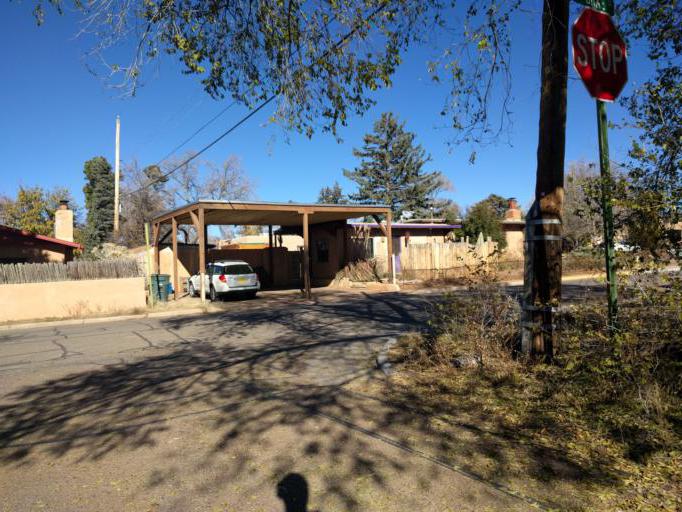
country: US
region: New Mexico
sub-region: Santa Fe County
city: Santa Fe
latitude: 35.6678
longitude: -105.9634
